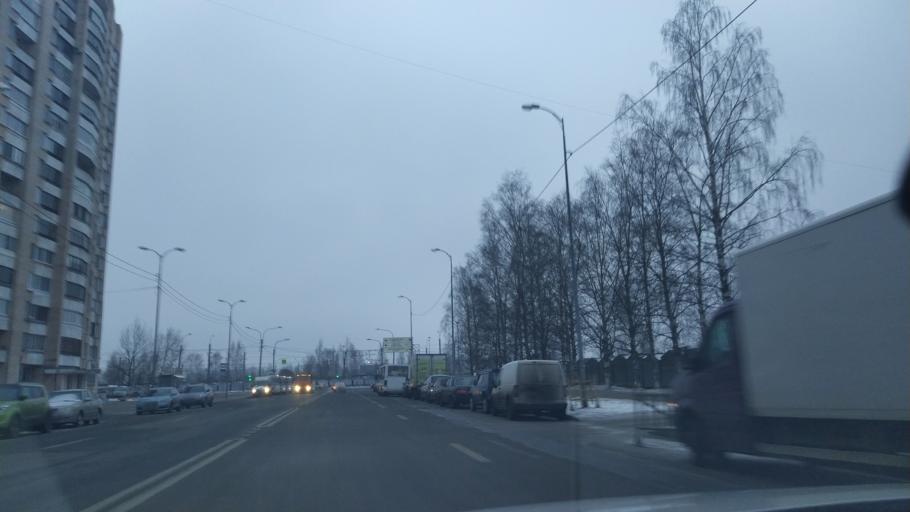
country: RU
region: St.-Petersburg
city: Grazhdanka
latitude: 60.0489
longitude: 30.3918
